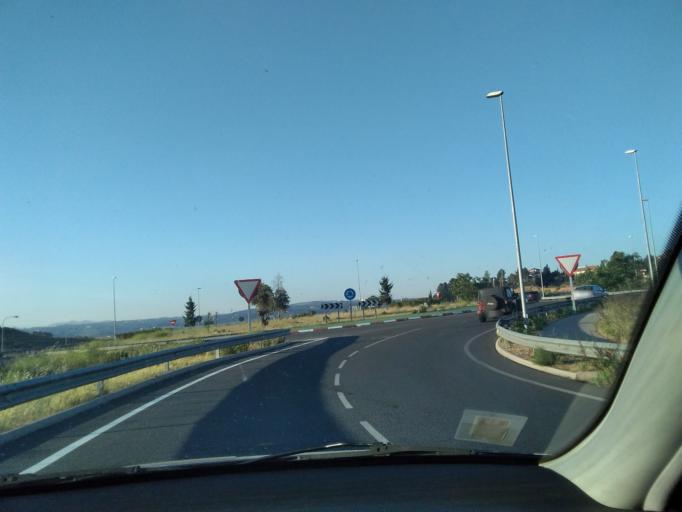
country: ES
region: Castille-La Mancha
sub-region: Province of Toledo
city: Toledo
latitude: 39.8885
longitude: -4.0553
